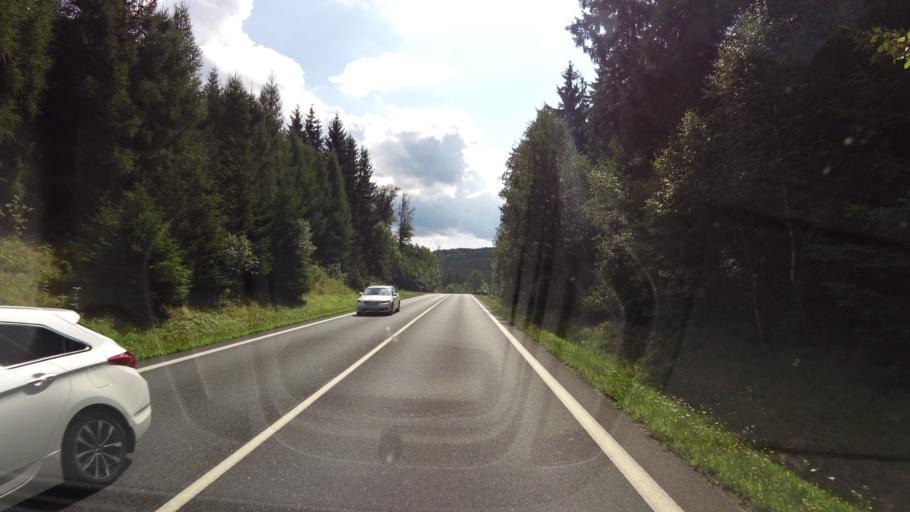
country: DE
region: Bavaria
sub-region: Upper Palatinate
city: Furth im Wald
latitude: 49.3753
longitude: 12.8534
